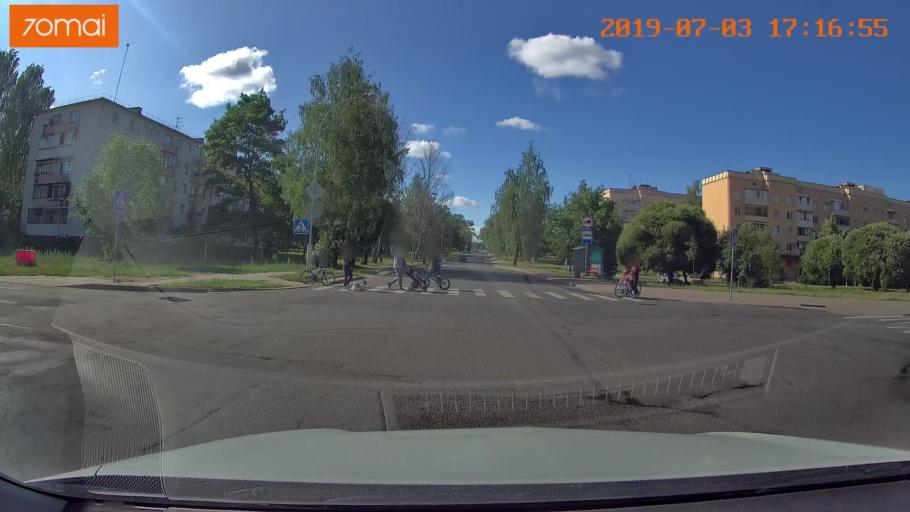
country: BY
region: Minsk
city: Vyaliki Trastsyanets
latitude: 53.9088
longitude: 27.6743
